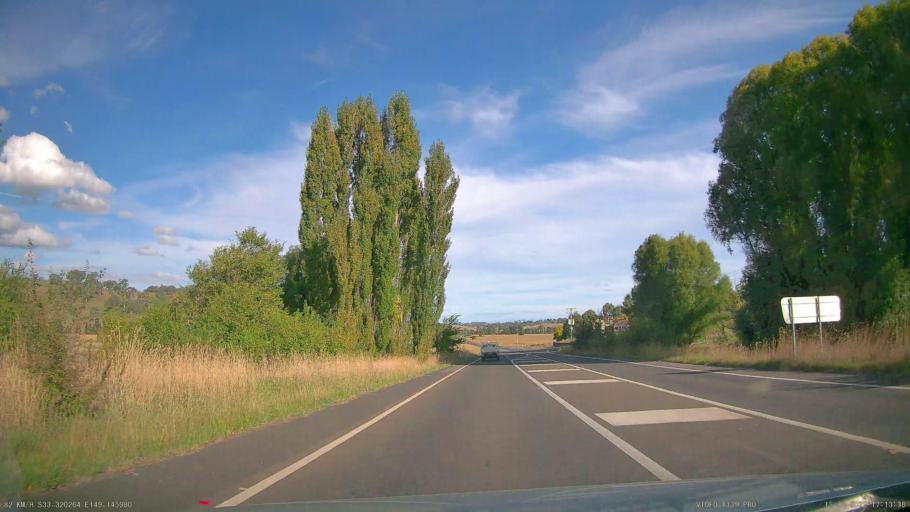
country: AU
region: New South Wales
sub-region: Orange Municipality
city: Orange
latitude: -33.3205
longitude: 149.1461
